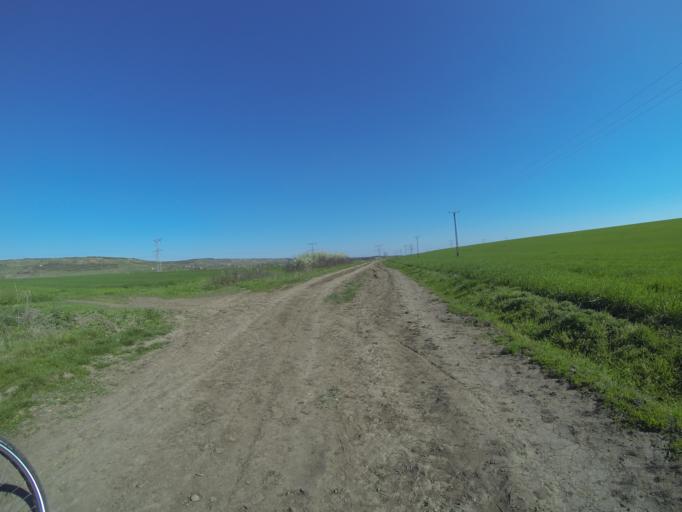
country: RO
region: Dolj
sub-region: Comuna Intorsura
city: Intorsura
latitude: 44.1259
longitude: 23.6068
